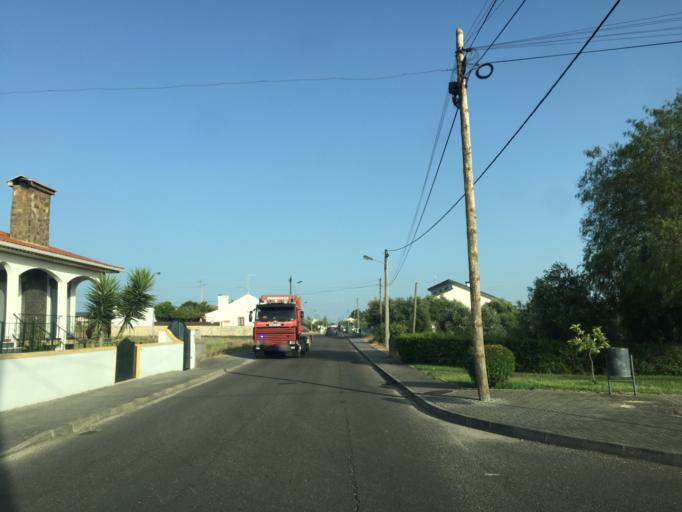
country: PT
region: Santarem
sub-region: Entroncamento
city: Entroncamento
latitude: 39.4760
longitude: -8.4503
